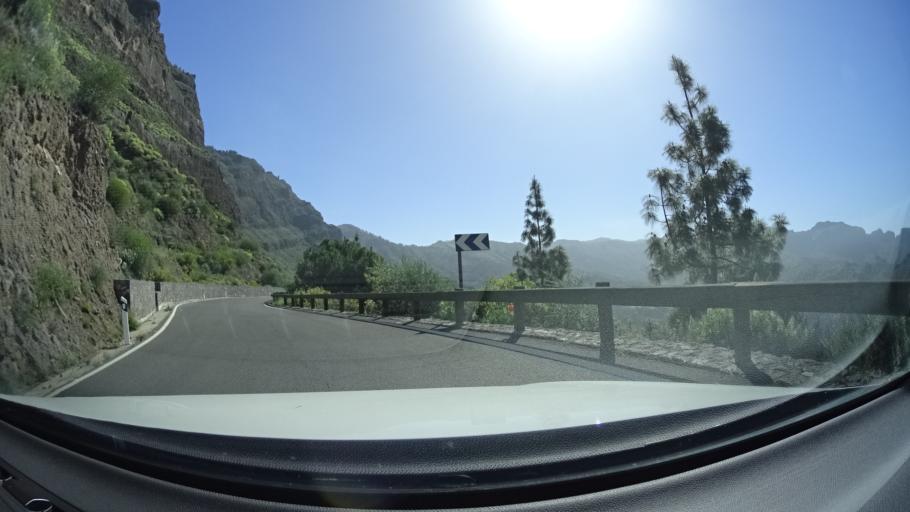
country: ES
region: Canary Islands
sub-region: Provincia de Las Palmas
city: Artenara
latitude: 28.0162
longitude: -15.6355
